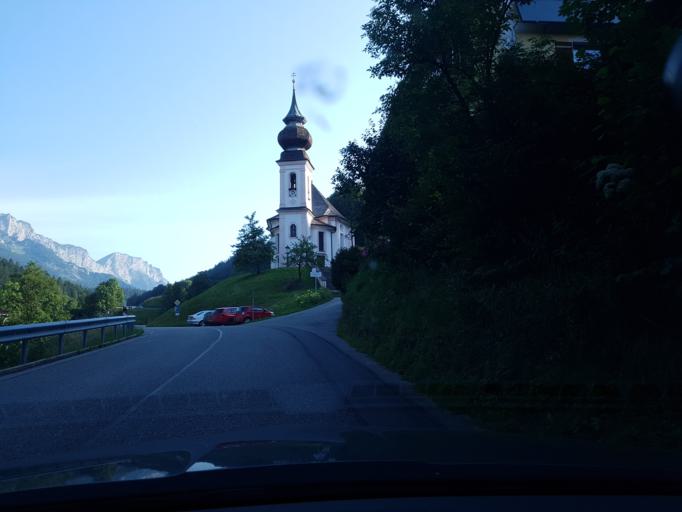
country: DE
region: Bavaria
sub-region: Upper Bavaria
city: Berchtesgaden
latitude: 47.6523
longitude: 13.0024
